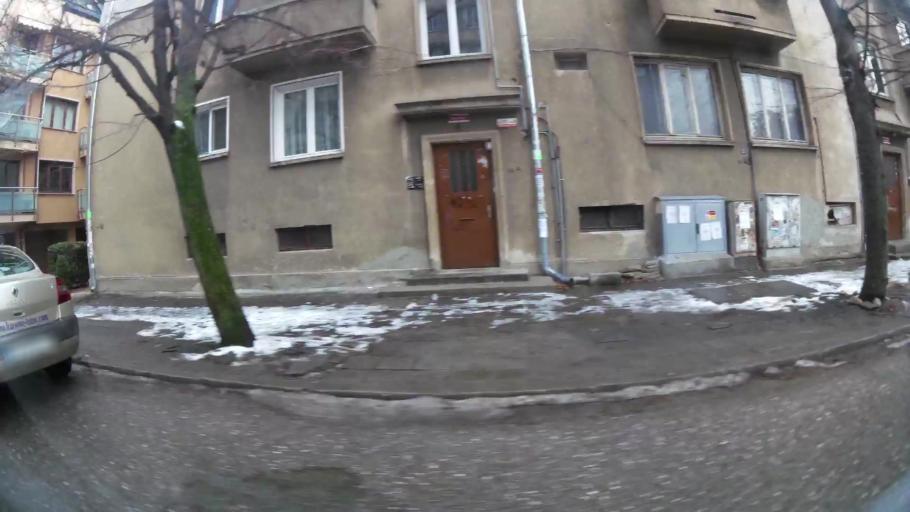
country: BG
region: Sofia-Capital
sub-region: Stolichna Obshtina
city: Sofia
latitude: 42.6807
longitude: 23.2978
